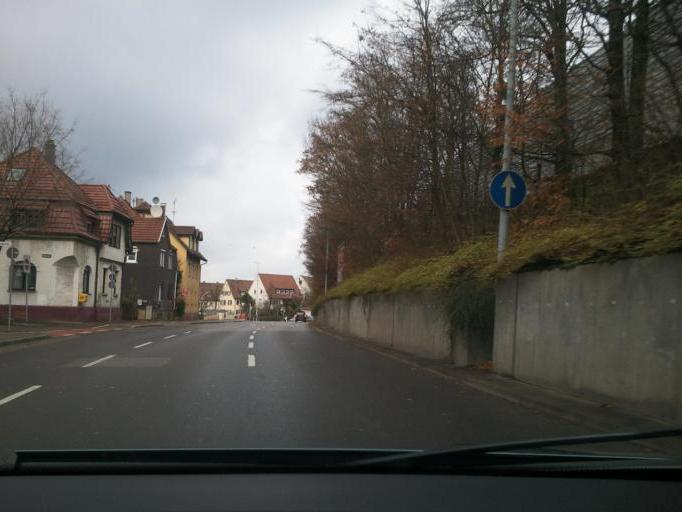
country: DE
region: Baden-Wuerttemberg
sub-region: Regierungsbezirk Stuttgart
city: Ludwigsburg
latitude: 48.9033
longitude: 9.1767
